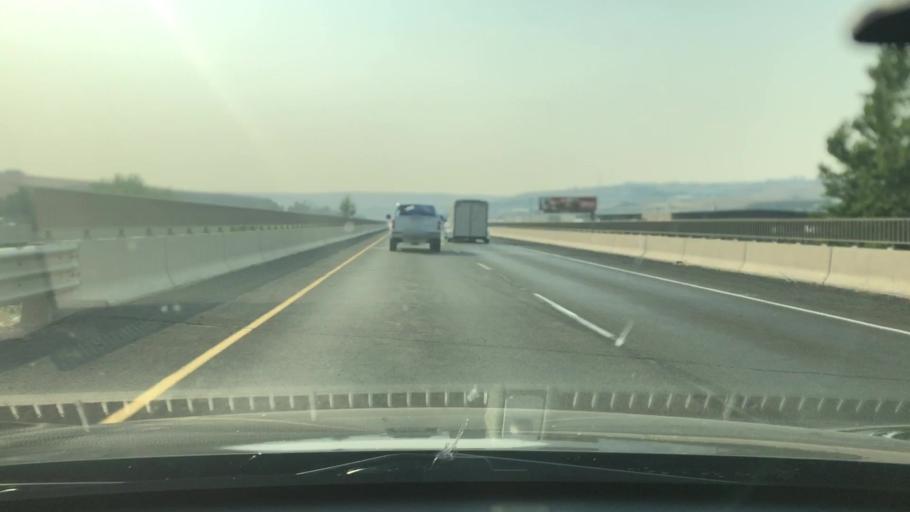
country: US
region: Oregon
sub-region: Umatilla County
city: Pendleton
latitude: 45.6664
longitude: -118.8158
